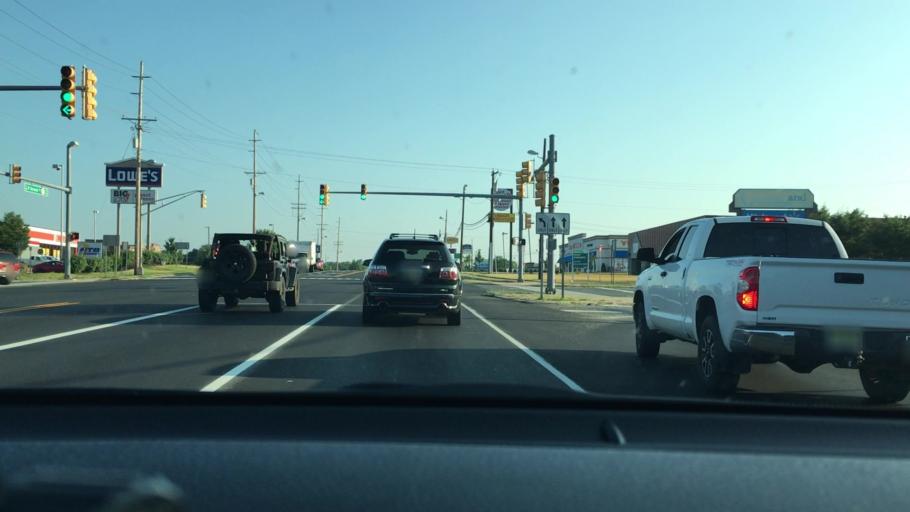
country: US
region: New Jersey
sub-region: Cumberland County
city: Millville
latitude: 39.4237
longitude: -75.0396
